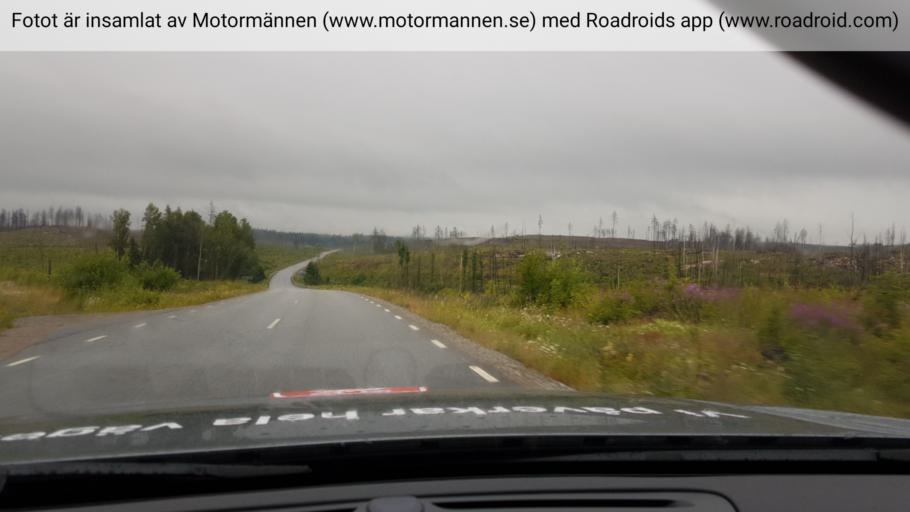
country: SE
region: Vaestmanland
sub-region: Norbergs Kommun
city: Norberg
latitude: 59.9833
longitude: 16.0494
